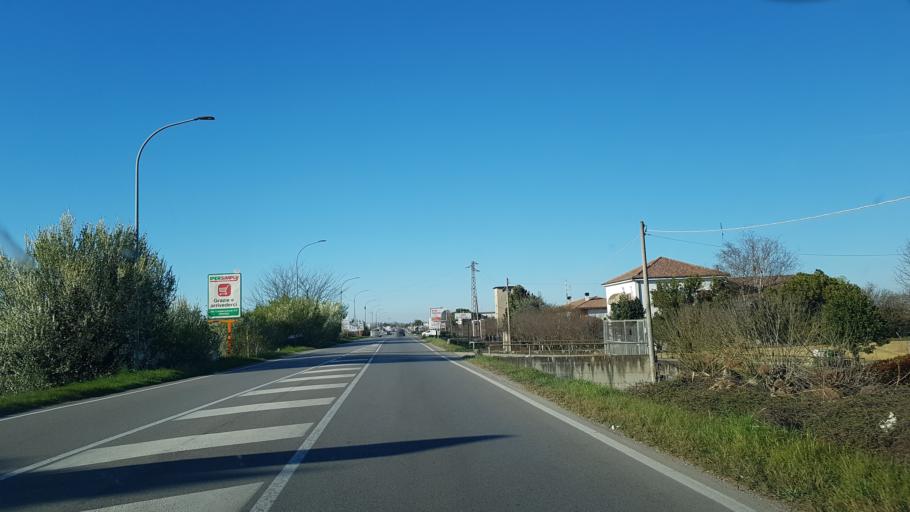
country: IT
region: Veneto
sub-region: Provincia di Rovigo
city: Rovigo
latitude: 45.0904
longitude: 11.7855
